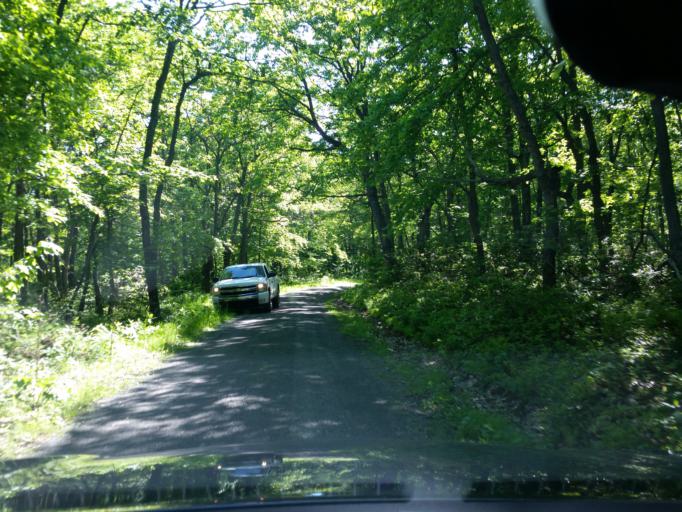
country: US
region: Pennsylvania
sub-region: Lycoming County
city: Duboistown
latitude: 41.1182
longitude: -77.1203
